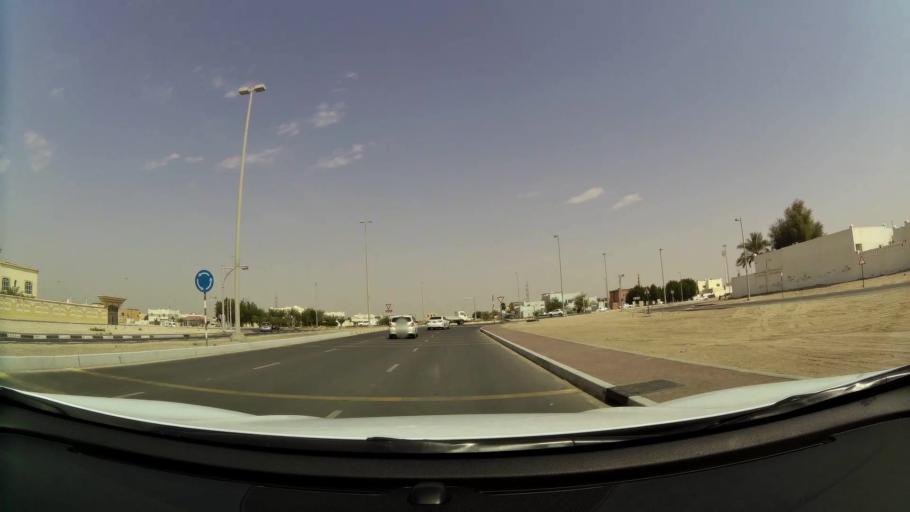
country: AE
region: Abu Dhabi
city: Abu Dhabi
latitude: 24.2992
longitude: 54.6476
